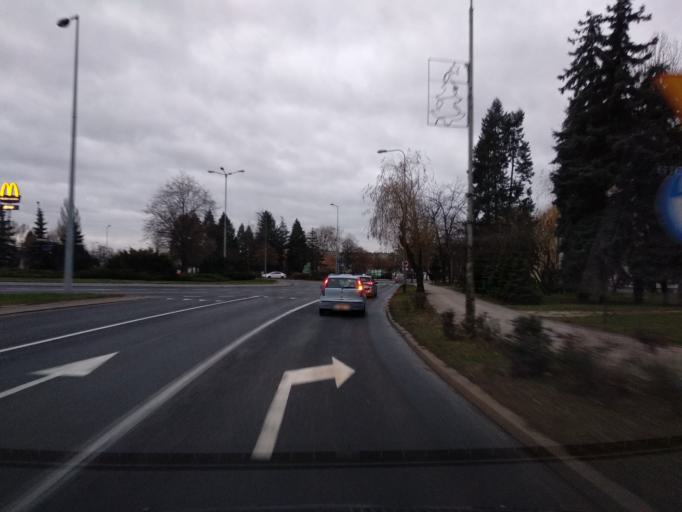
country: PL
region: Greater Poland Voivodeship
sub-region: Konin
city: Konin
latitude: 52.2281
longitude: 18.2628
